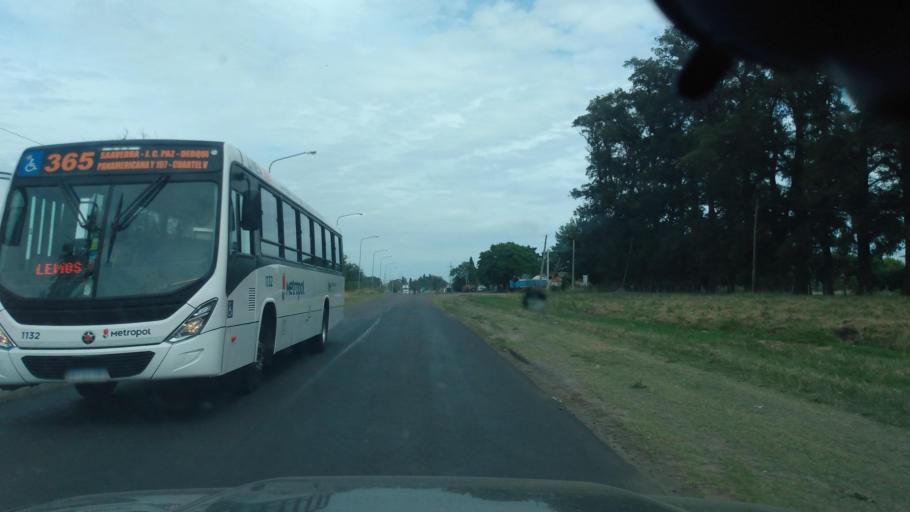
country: AR
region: Buenos Aires
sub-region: Partido de Lujan
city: Lujan
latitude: -34.5794
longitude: -59.0777
